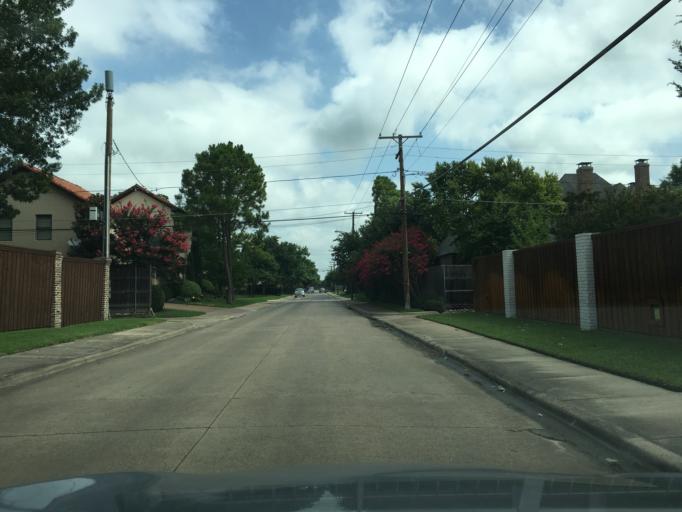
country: US
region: Texas
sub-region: Dallas County
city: University Park
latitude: 32.8875
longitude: -96.7931
